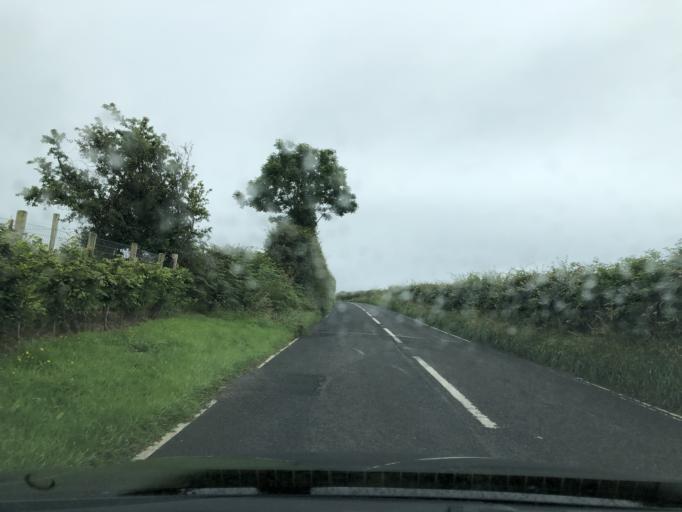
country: GB
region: Northern Ireland
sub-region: Down District
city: Dundrum
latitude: 54.2798
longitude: -5.8094
